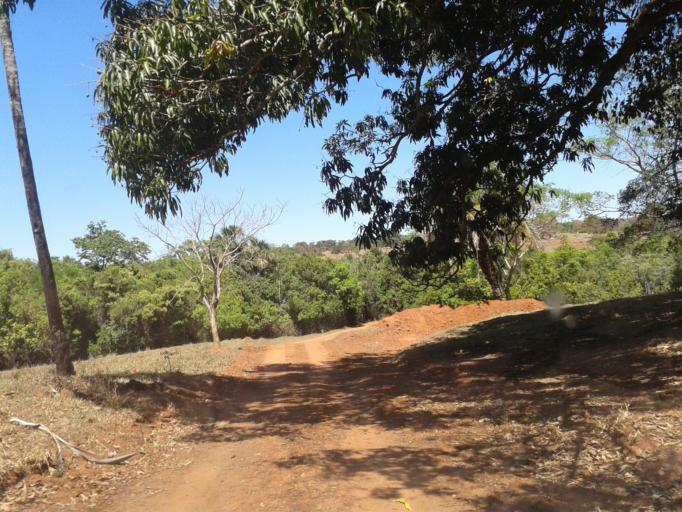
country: BR
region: Minas Gerais
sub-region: Ituiutaba
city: Ituiutaba
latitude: -19.1117
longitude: -49.2757
